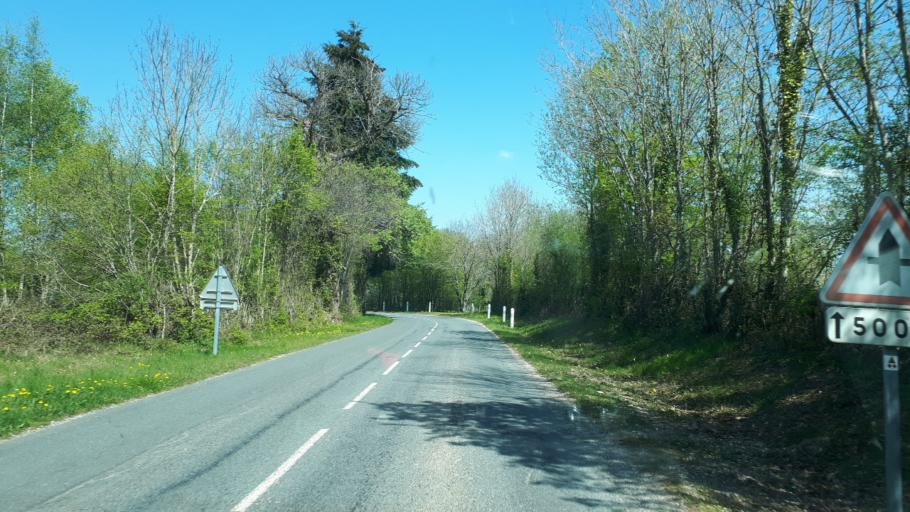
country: FR
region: Centre
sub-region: Departement du Cher
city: Henrichemont
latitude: 47.3028
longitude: 2.6204
